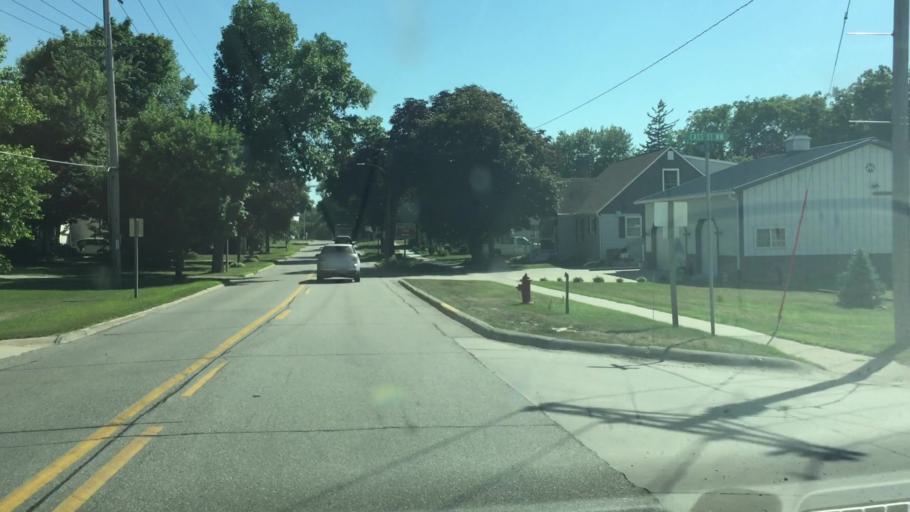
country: US
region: Iowa
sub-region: Linn County
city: Mount Vernon
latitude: 41.9287
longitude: -91.4107
